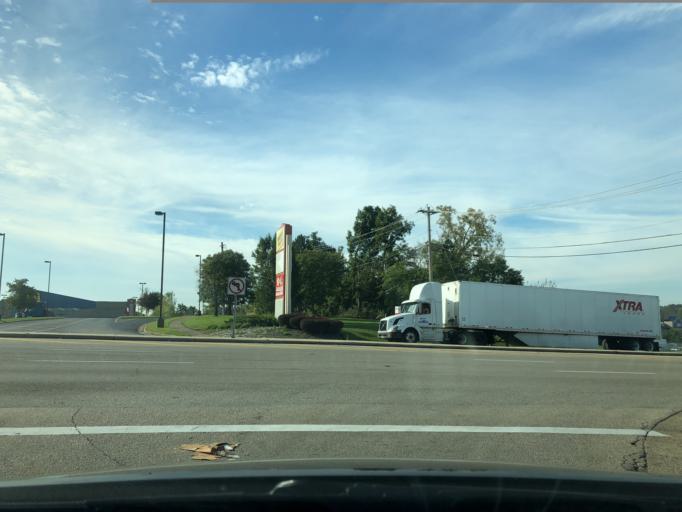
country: US
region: Ohio
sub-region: Hamilton County
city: Glendale
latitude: 39.2872
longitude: -84.4556
